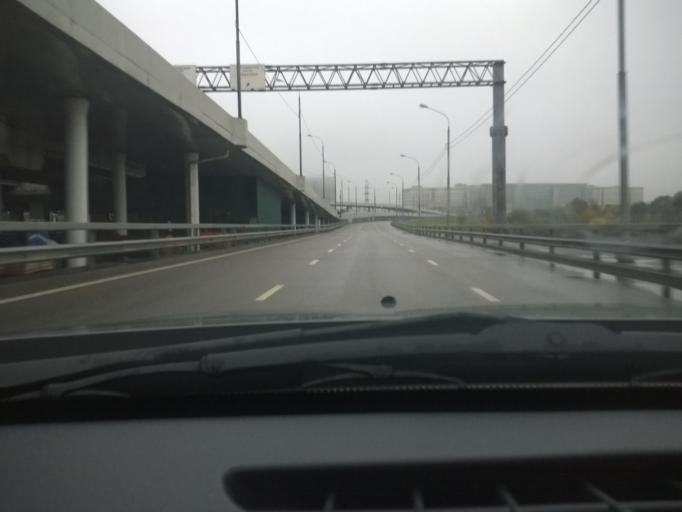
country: RU
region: Moscow
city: Zhulebino
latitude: 55.7113
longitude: 37.8443
